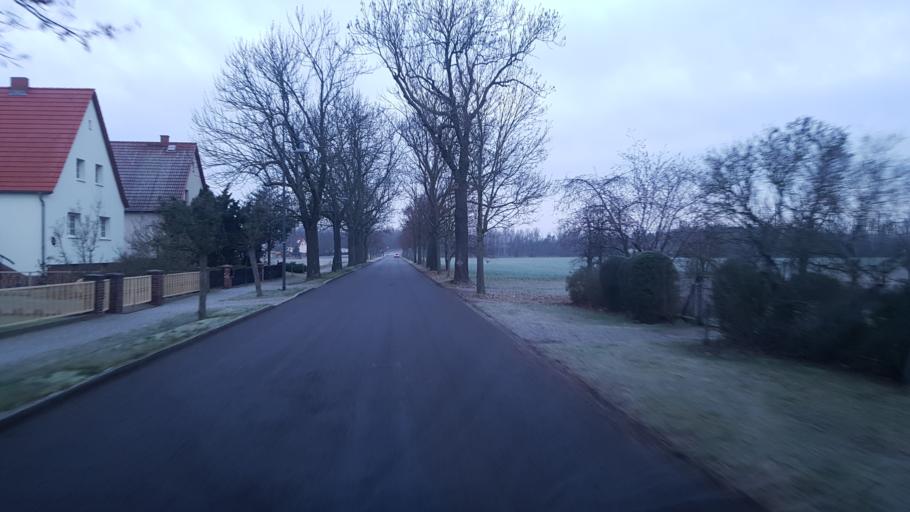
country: DE
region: Brandenburg
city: Ludwigsfelde
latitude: 52.3146
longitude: 13.2041
